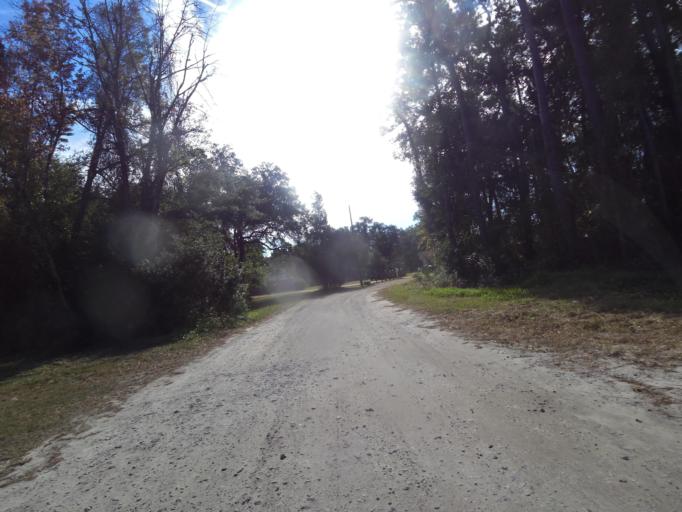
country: US
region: Georgia
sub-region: Glynn County
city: Brunswick
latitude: 31.1427
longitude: -81.5693
